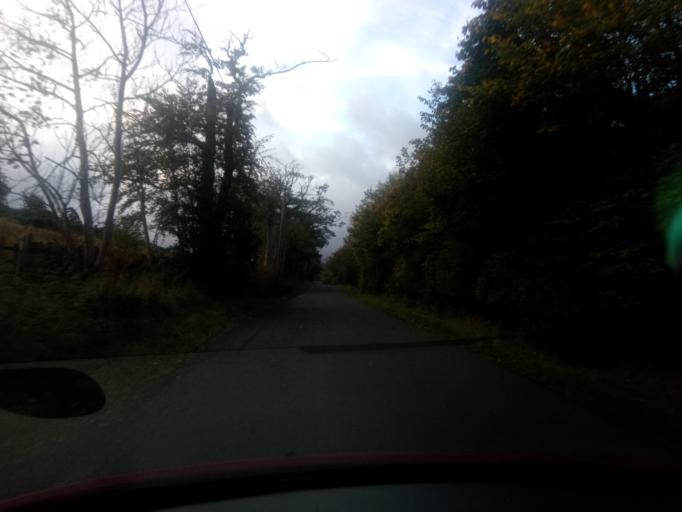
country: GB
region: Scotland
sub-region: The Scottish Borders
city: Jedburgh
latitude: 55.3721
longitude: -2.6487
